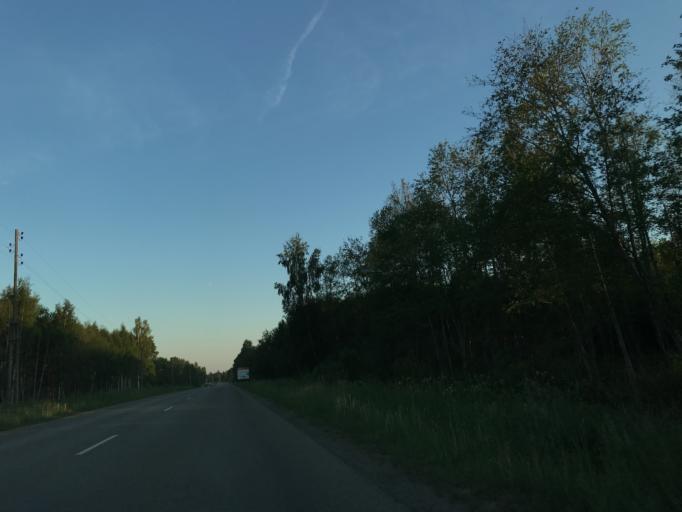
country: LV
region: Jaunjelgava
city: Jaunjelgava
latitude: 56.4315
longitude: 24.9244
